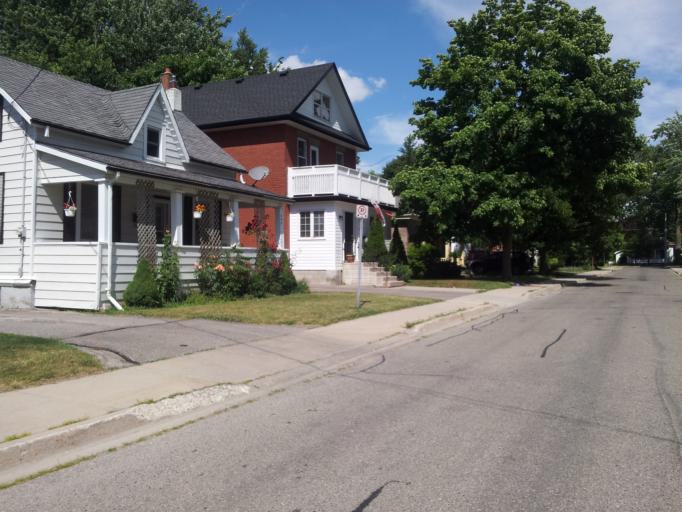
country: CA
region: Ontario
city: Stratford
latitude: 43.3690
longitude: -80.9749
